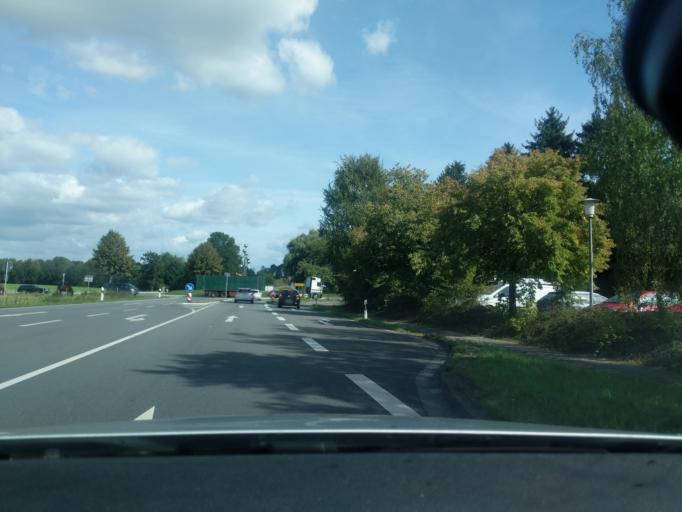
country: DE
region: Lower Saxony
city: Laar
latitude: 52.3461
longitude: 8.2532
